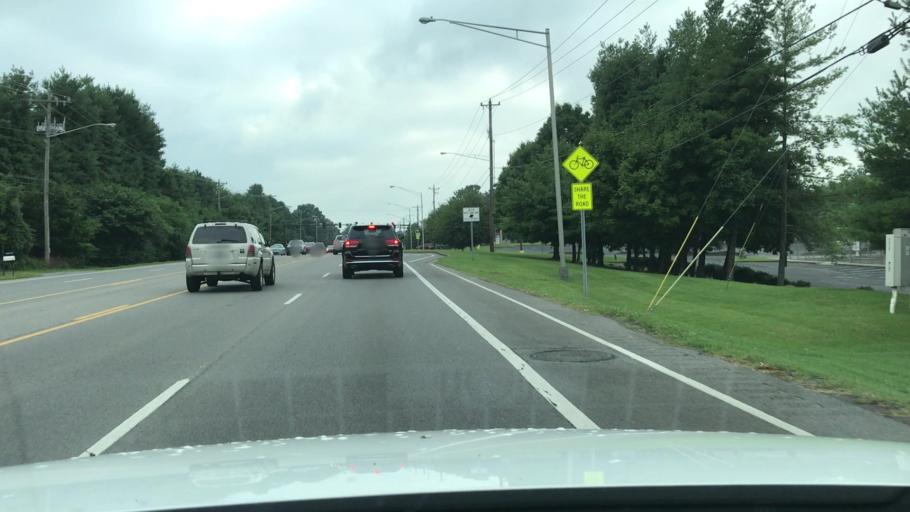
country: US
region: Tennessee
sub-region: Sumner County
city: Hendersonville
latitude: 36.3143
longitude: -86.5912
